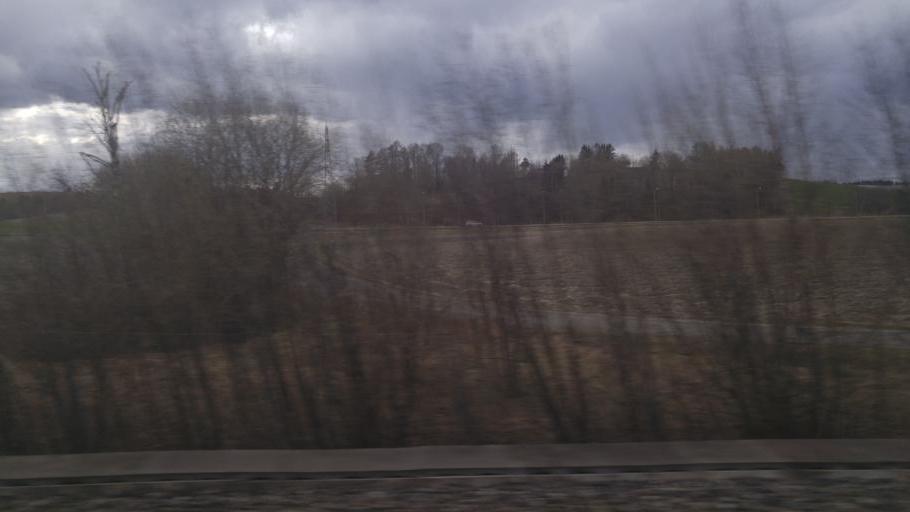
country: NO
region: Akershus
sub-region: Skedsmo
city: Leirsund
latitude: 59.9831
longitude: 11.0743
